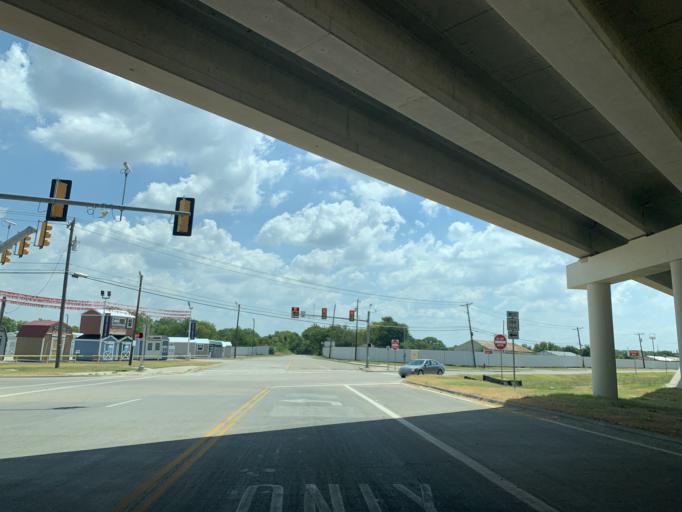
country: US
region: Texas
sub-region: Tarrant County
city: Lakeside
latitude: 32.8380
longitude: -97.4917
